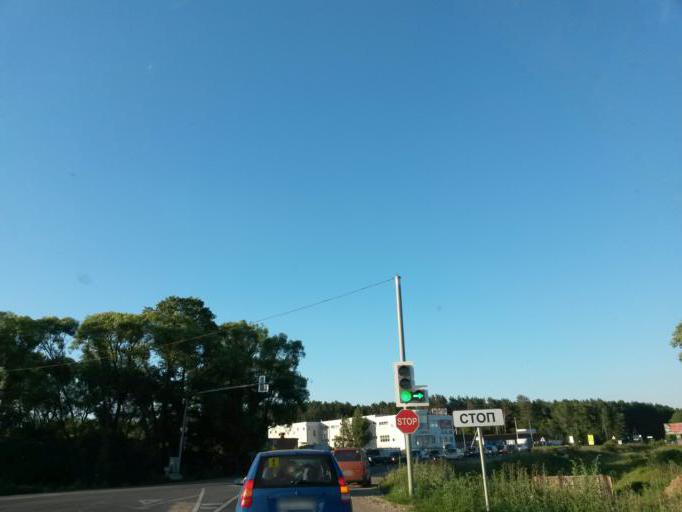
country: RU
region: Moskovskaya
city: Protvino
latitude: 54.8902
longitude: 37.2946
